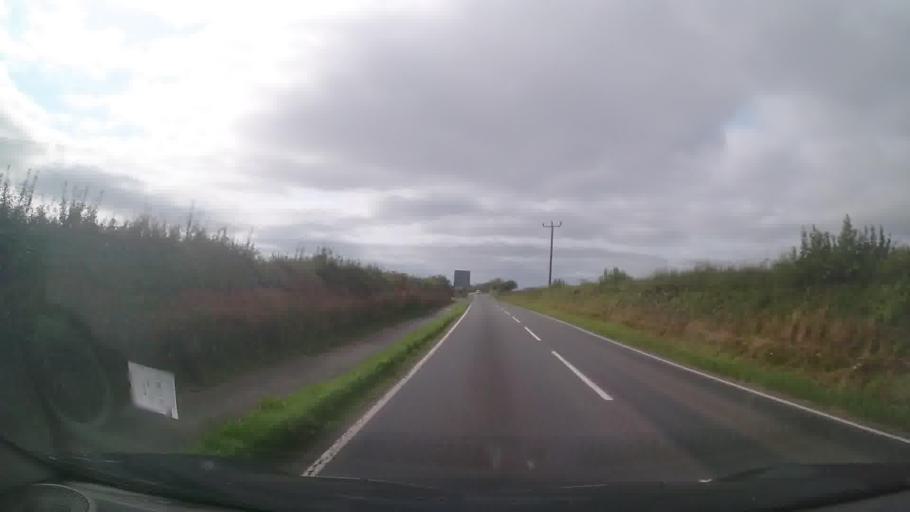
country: GB
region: Wales
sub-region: Pembrokeshire
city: Steynton
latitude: 51.7315
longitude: -4.9932
